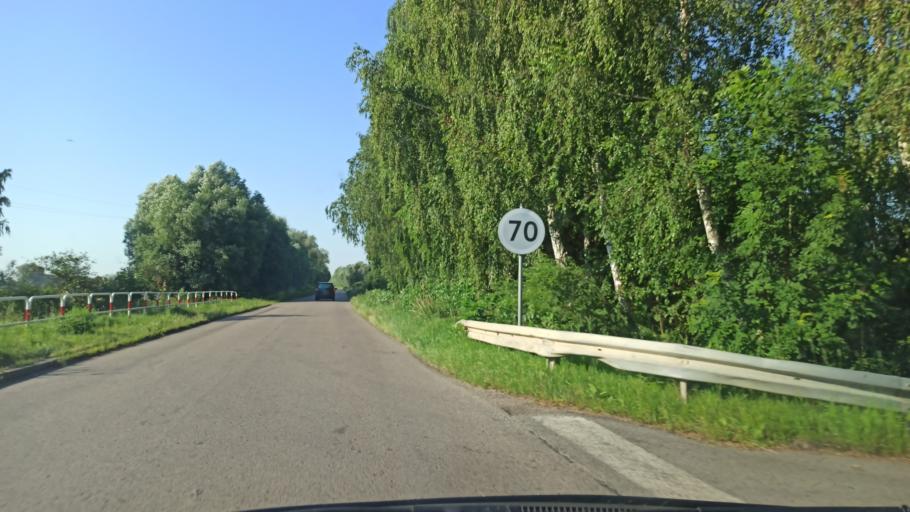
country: PL
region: Warmian-Masurian Voivodeship
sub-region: Powiat elblaski
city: Elblag
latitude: 54.1741
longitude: 19.3313
